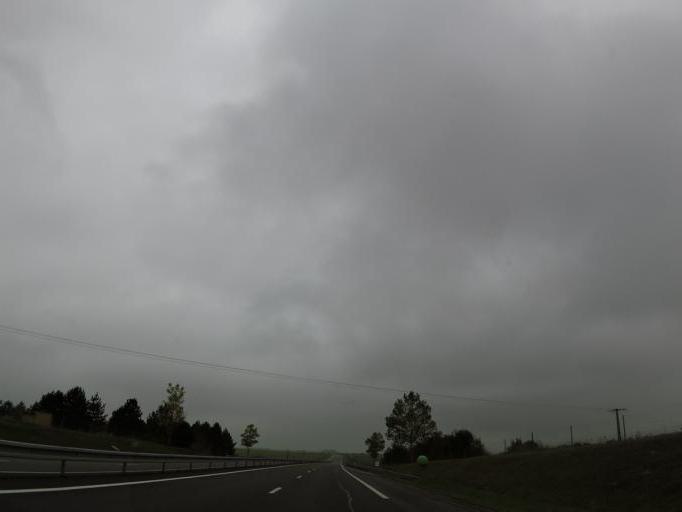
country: FR
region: Champagne-Ardenne
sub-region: Departement de la Marne
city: Courtisols
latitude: 49.0361
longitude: 4.5869
